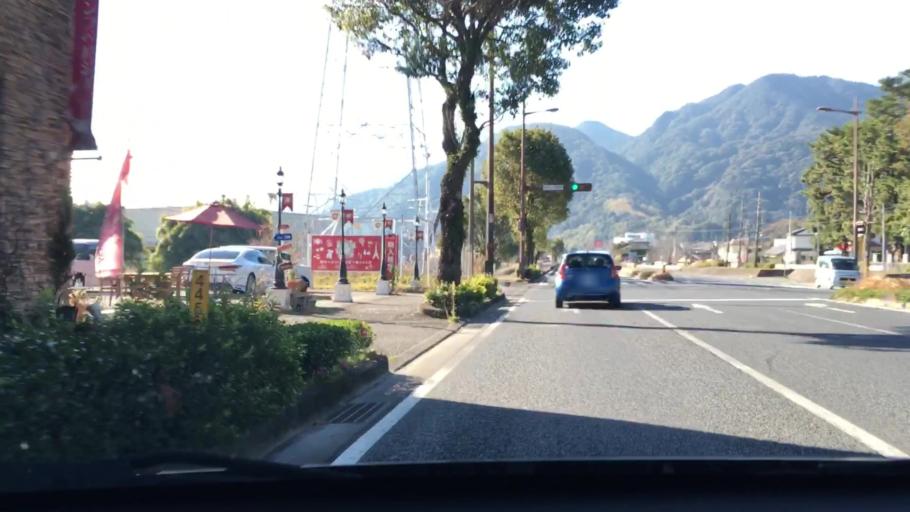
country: JP
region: Kagoshima
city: Kajiki
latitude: 31.7135
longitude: 130.6176
